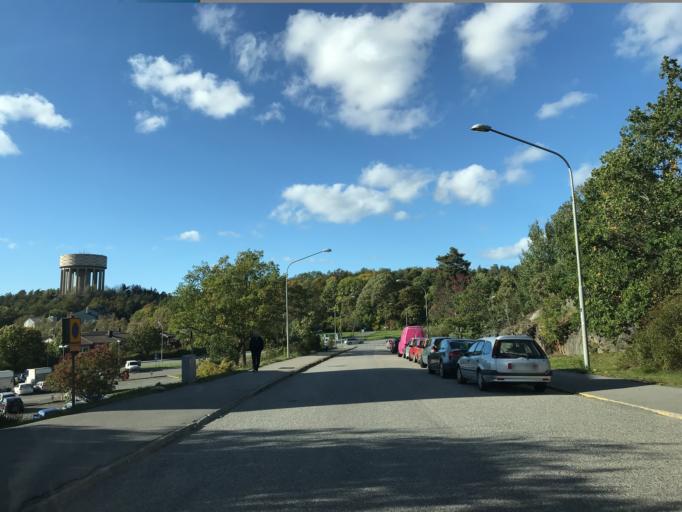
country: SE
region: Stockholm
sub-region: Huddinge Kommun
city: Segeltorp
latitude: 59.2867
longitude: 17.9142
